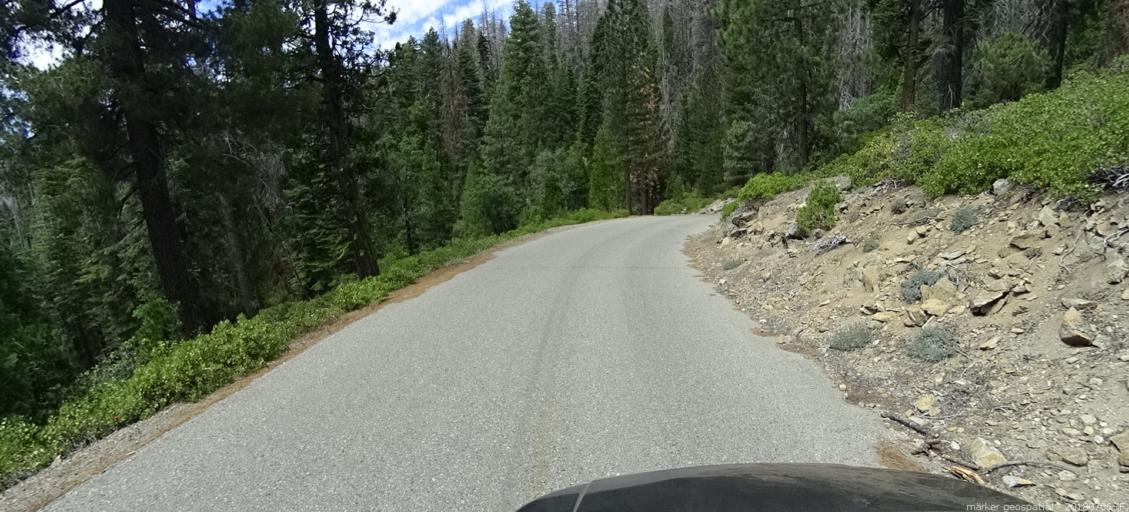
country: US
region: California
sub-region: Madera County
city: Oakhurst
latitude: 37.4274
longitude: -119.4122
